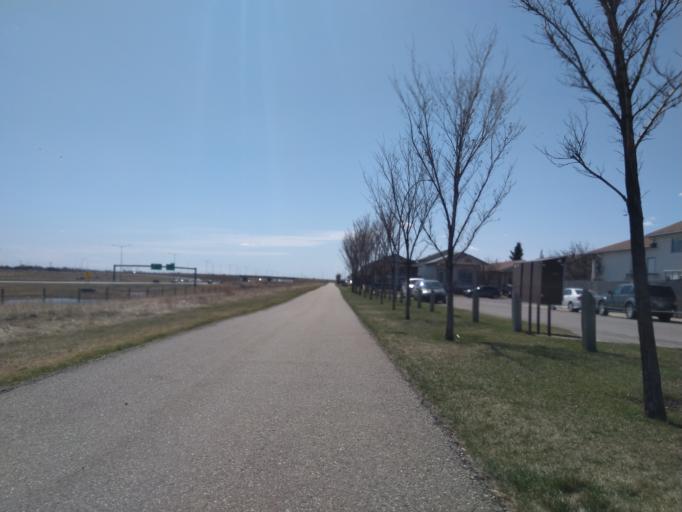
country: CA
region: Alberta
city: Chestermere
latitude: 51.0460
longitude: -113.9228
